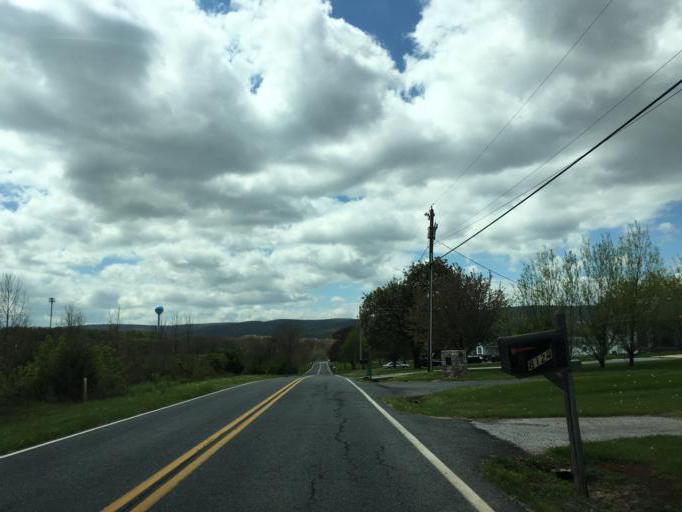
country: US
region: Maryland
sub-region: Frederick County
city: Thurmont
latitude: 39.6281
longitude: -77.3839
